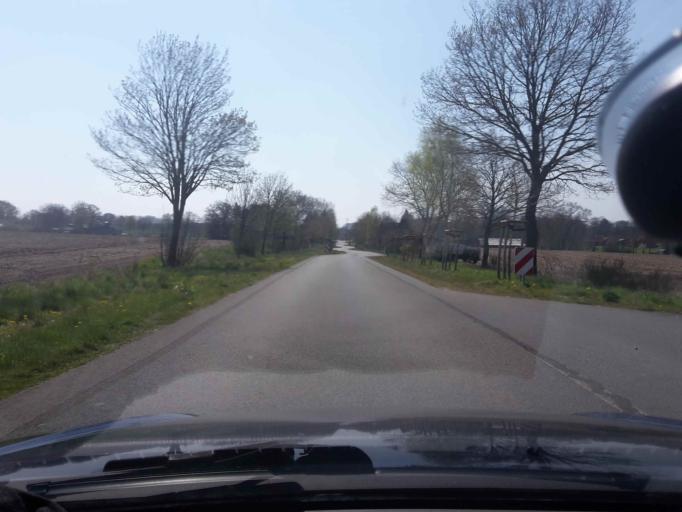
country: DE
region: Lower Saxony
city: Schneverdingen
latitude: 53.0859
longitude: 9.8614
